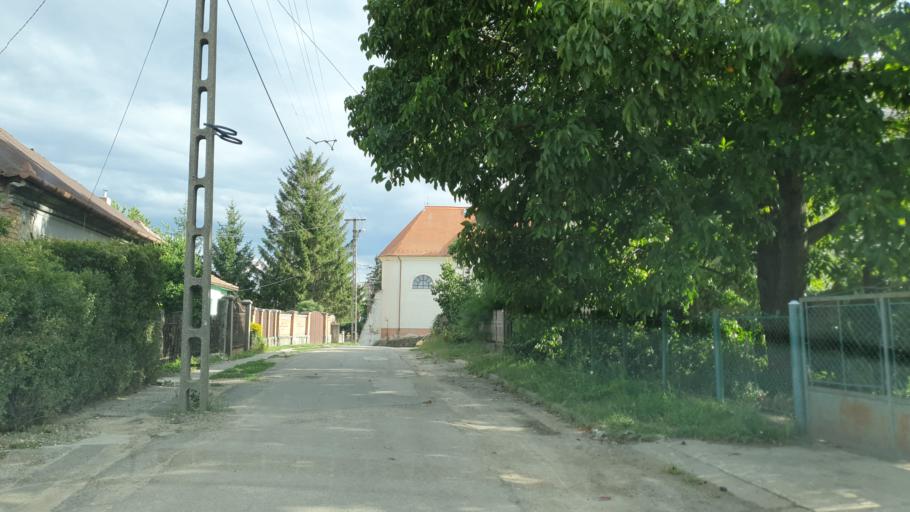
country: HU
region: Nograd
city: Jobbagyi
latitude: 47.8306
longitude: 19.6764
